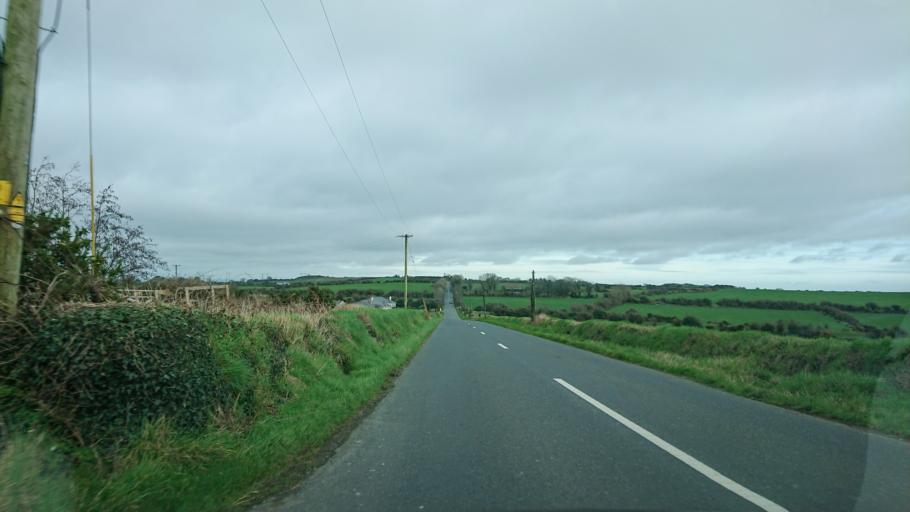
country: IE
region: Munster
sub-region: Waterford
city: Portlaw
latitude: 52.1876
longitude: -7.2903
